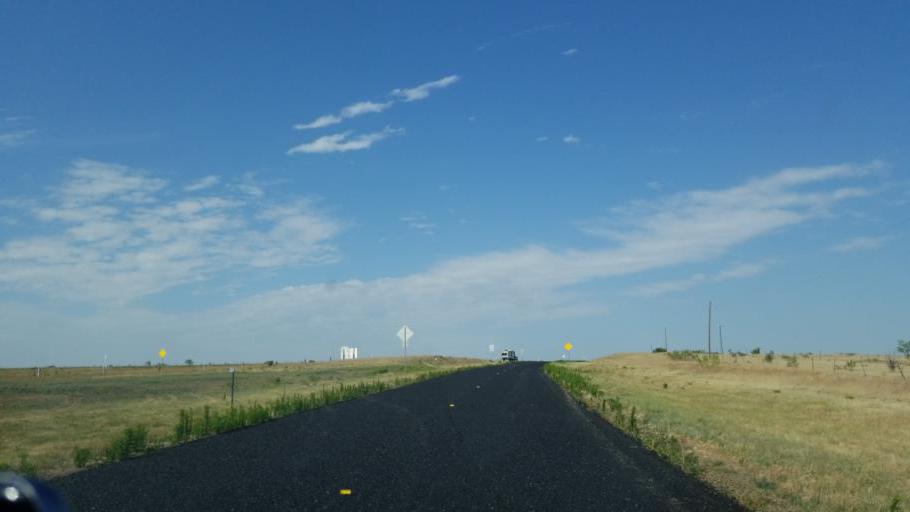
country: US
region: Texas
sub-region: Oldham County
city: Vega
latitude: 35.2579
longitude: -102.7625
